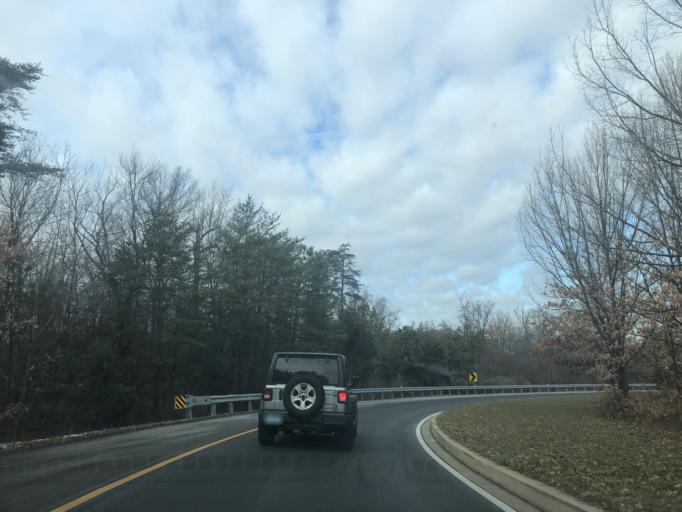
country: US
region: Maryland
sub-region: Howard County
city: Hanover
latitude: 39.1696
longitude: -76.7329
